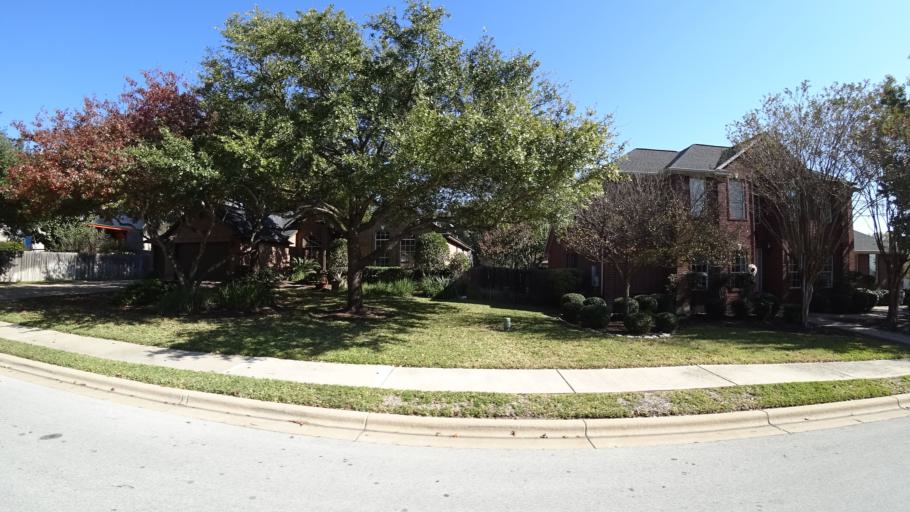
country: US
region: Texas
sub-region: Travis County
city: Lost Creek
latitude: 30.3743
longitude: -97.8481
